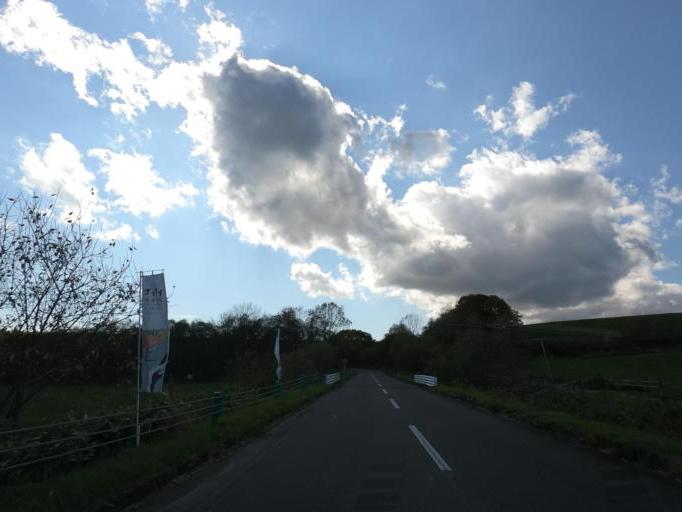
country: JP
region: Hokkaido
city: Otofuke
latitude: 43.2831
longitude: 143.2363
